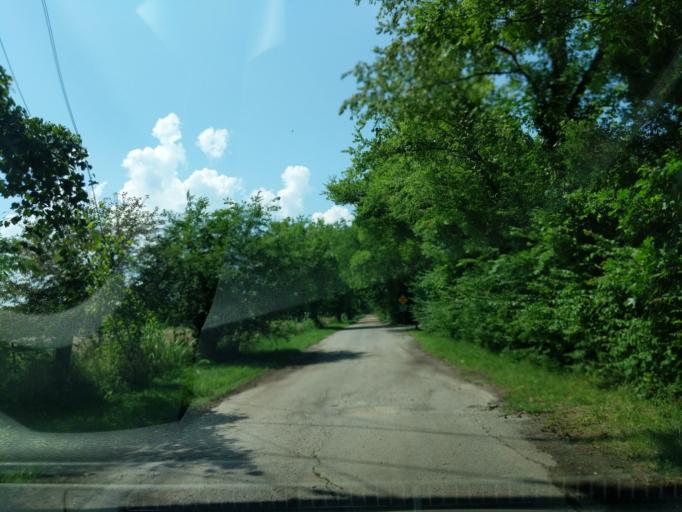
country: US
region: Tennessee
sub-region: Davidson County
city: Goodlettsville
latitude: 36.2860
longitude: -86.6797
